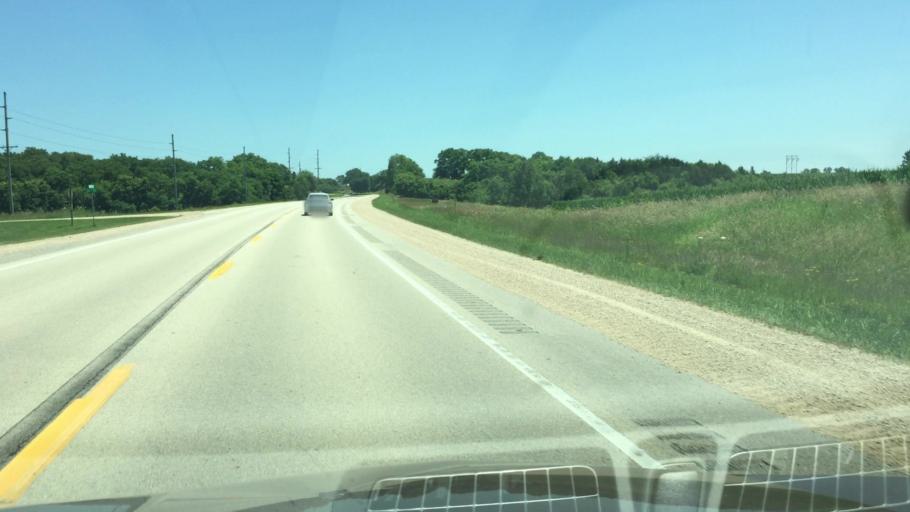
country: US
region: Iowa
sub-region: Jackson County
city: Maquoketa
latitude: 42.0638
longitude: -90.7626
